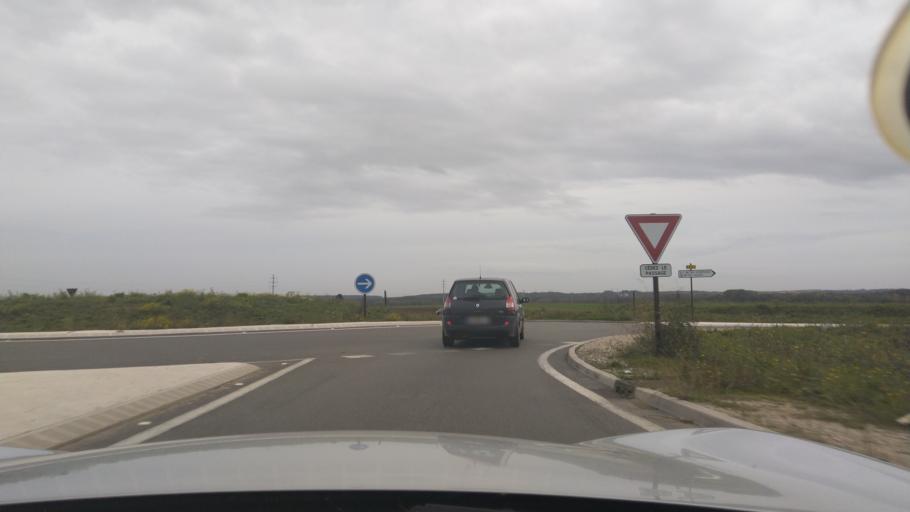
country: FR
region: Ile-de-France
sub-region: Departement de Seine-et-Marne
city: Claye-Souilly
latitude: 48.9780
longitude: 2.6601
